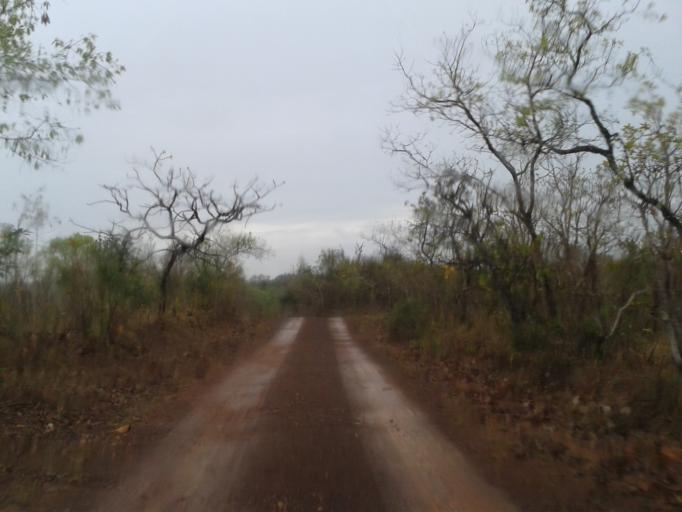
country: BR
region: Minas Gerais
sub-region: Campina Verde
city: Campina Verde
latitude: -19.3206
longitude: -49.5120
